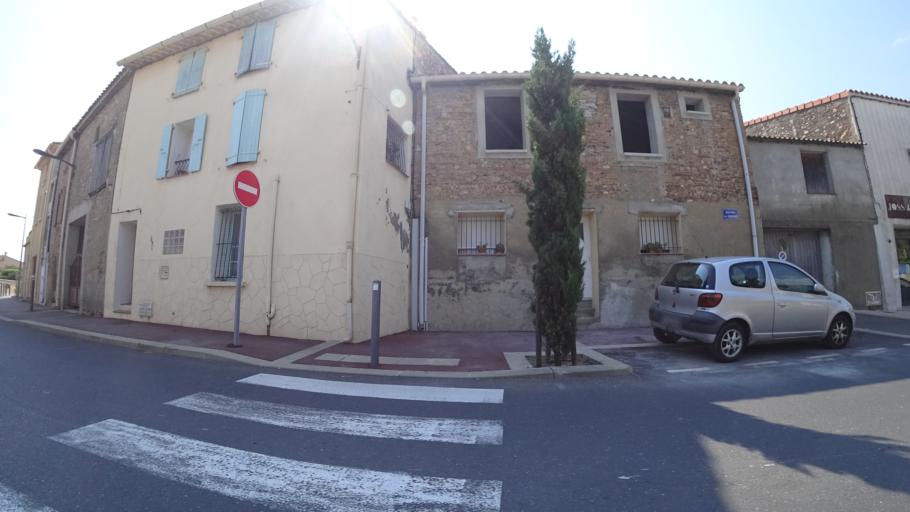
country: FR
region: Languedoc-Roussillon
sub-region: Departement des Pyrenees-Orientales
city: Villelongue-de-la-Salanque
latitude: 42.7278
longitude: 2.9829
